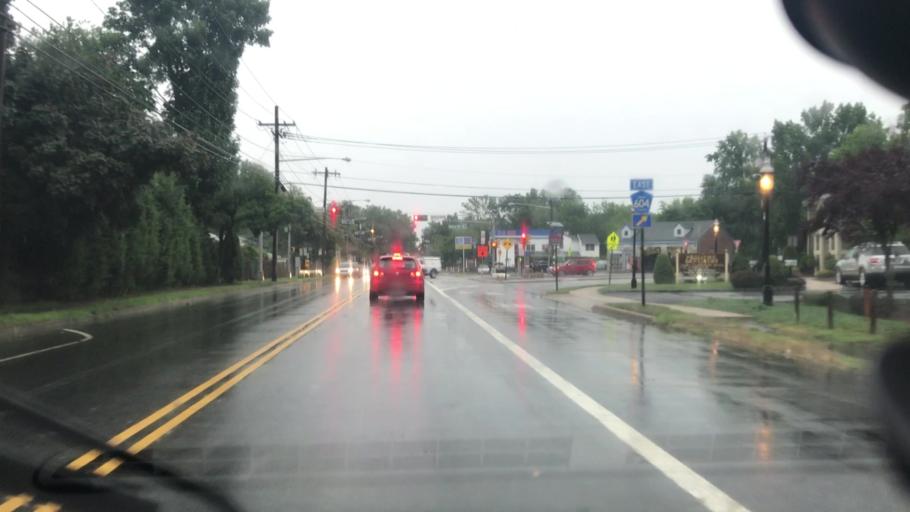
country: US
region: New Jersey
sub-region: Union County
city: Clark
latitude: 40.6184
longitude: -74.3228
